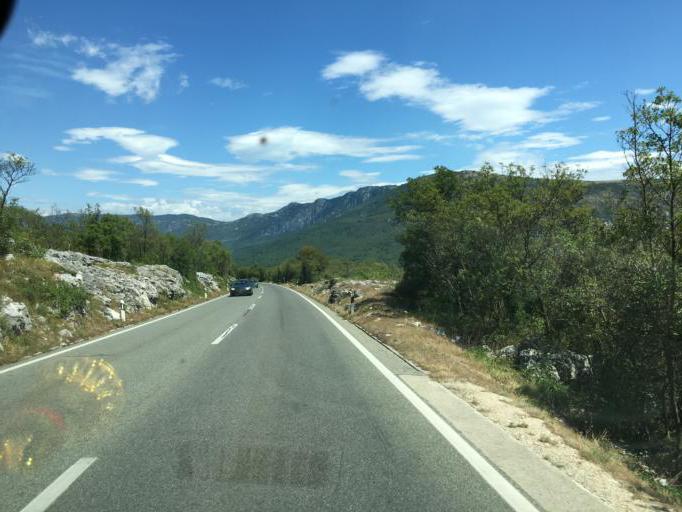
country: HR
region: Istarska
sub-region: Grad Labin
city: Labin
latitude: 45.1371
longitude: 14.1440
